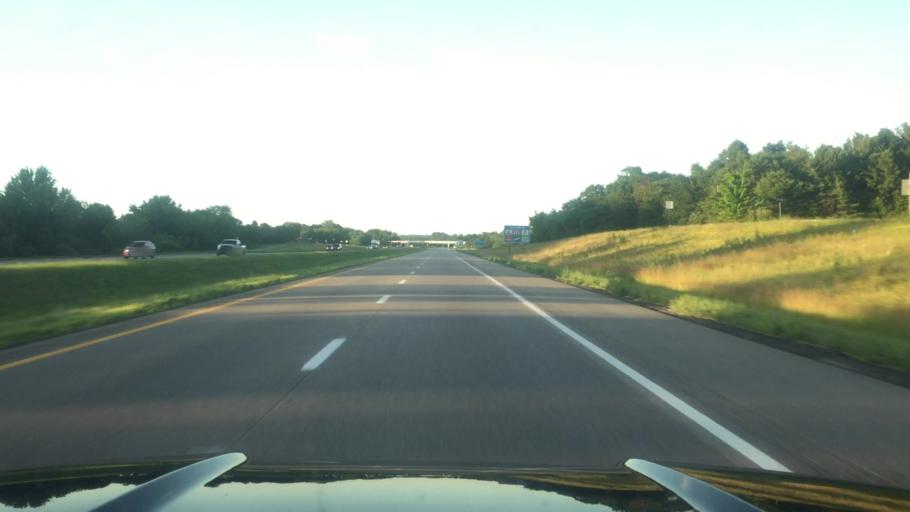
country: US
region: Ohio
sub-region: Tuscarawas County
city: Strasburg
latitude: 40.6233
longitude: -81.4681
